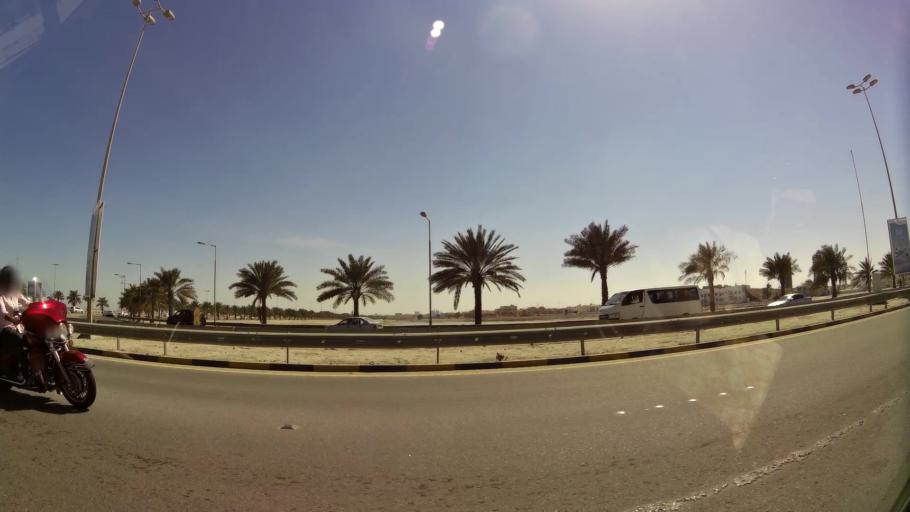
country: BH
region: Muharraq
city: Al Hadd
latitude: 26.2544
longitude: 50.6589
